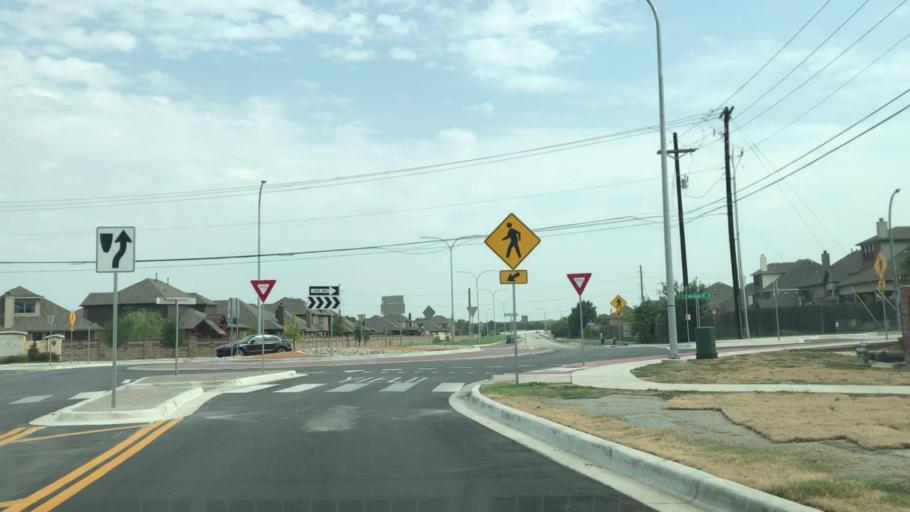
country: US
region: Texas
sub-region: Tarrant County
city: Keller
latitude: 32.9237
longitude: -97.2725
